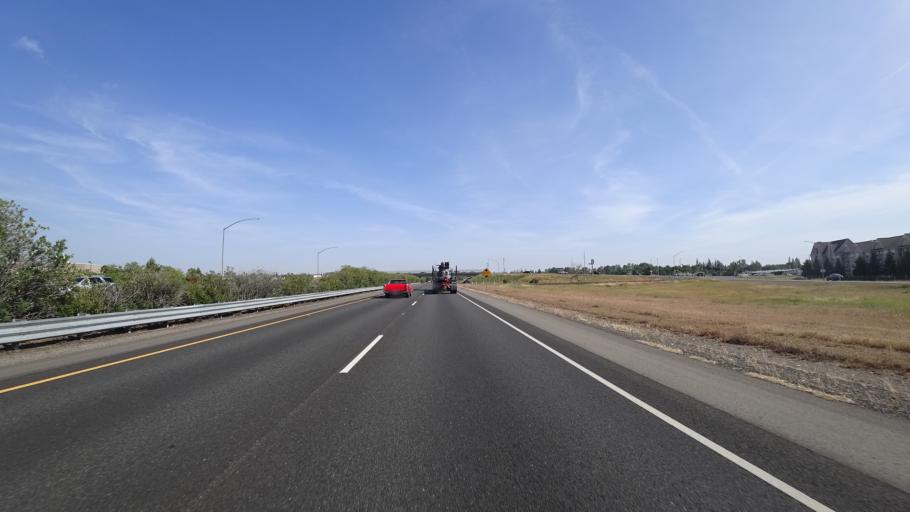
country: US
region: California
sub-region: Butte County
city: Chico
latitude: 39.7170
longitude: -121.8024
